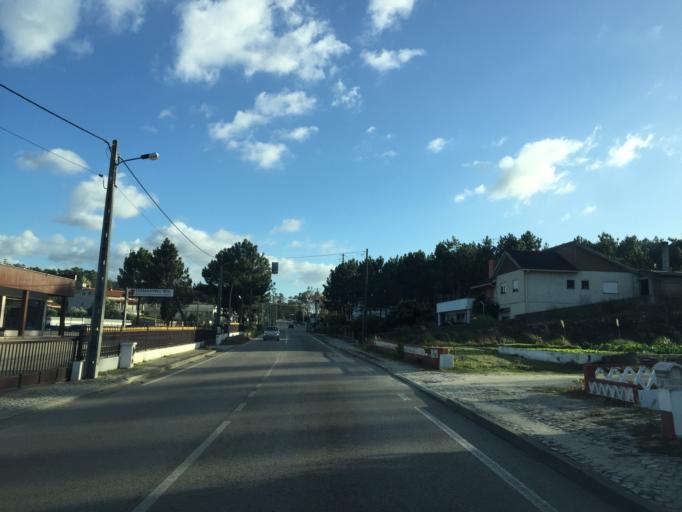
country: PT
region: Leiria
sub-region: Leiria
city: Souto da Carpalhosa
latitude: 39.8269
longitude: -8.8402
